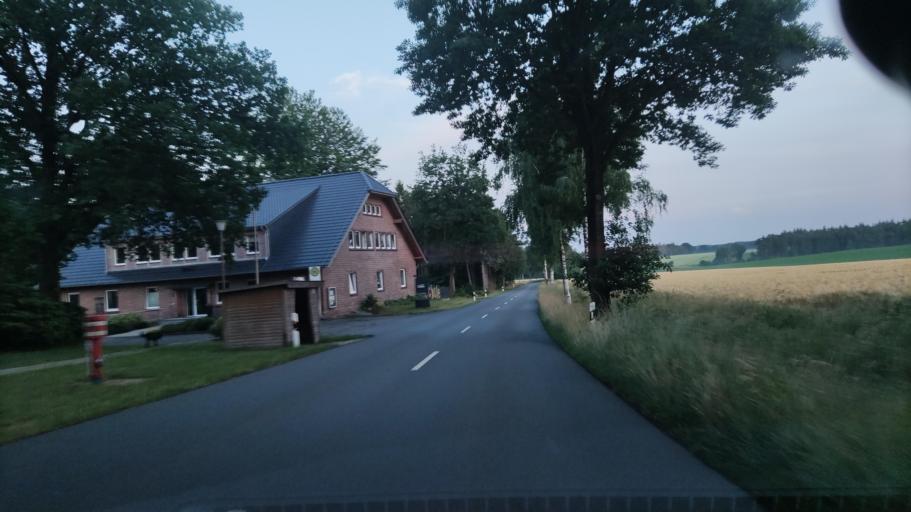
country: DE
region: Lower Saxony
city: Bispingen
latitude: 53.1224
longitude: 10.0533
